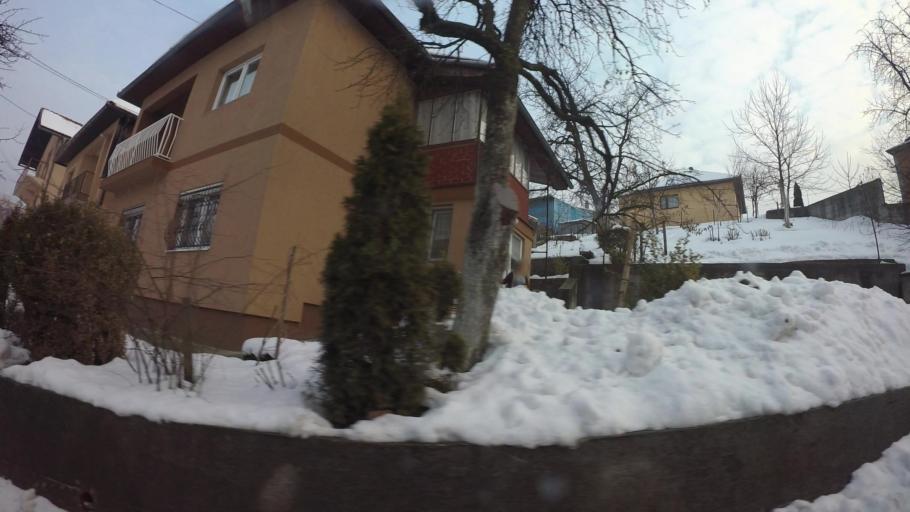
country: BA
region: Federation of Bosnia and Herzegovina
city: Hotonj
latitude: 43.8957
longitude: 18.3728
